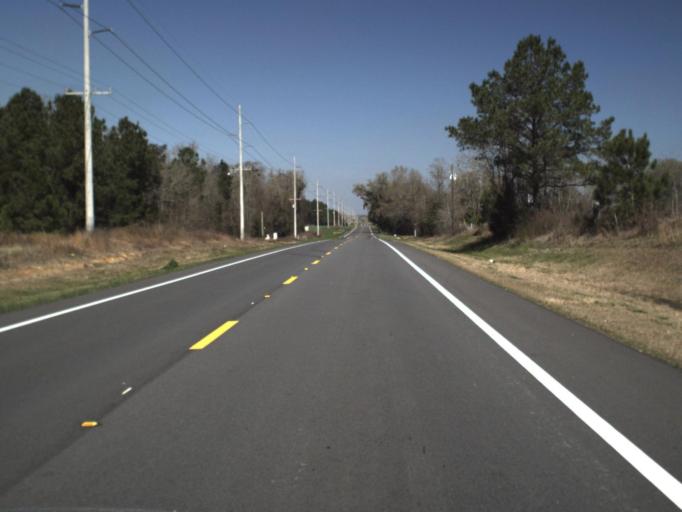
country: US
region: Florida
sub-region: Jackson County
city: Sneads
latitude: 30.7570
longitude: -85.0194
